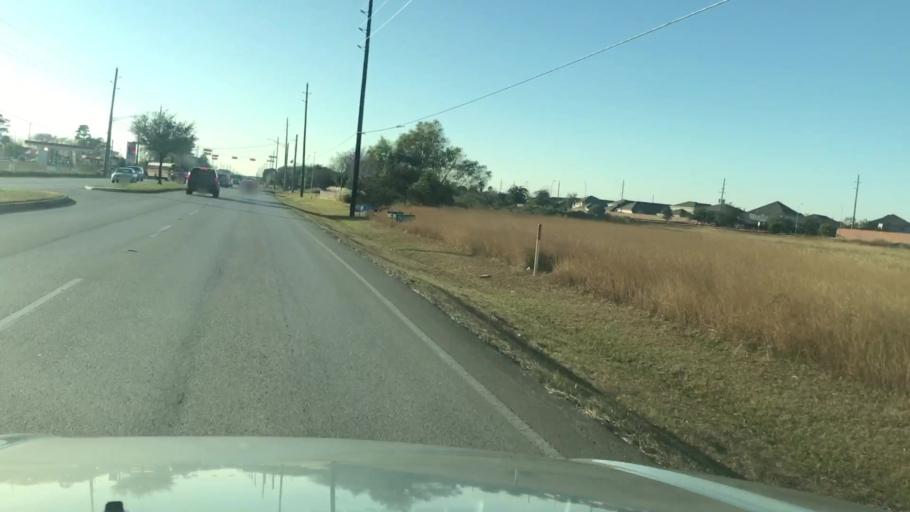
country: US
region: Texas
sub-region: Harris County
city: Katy
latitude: 29.8319
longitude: -95.7440
